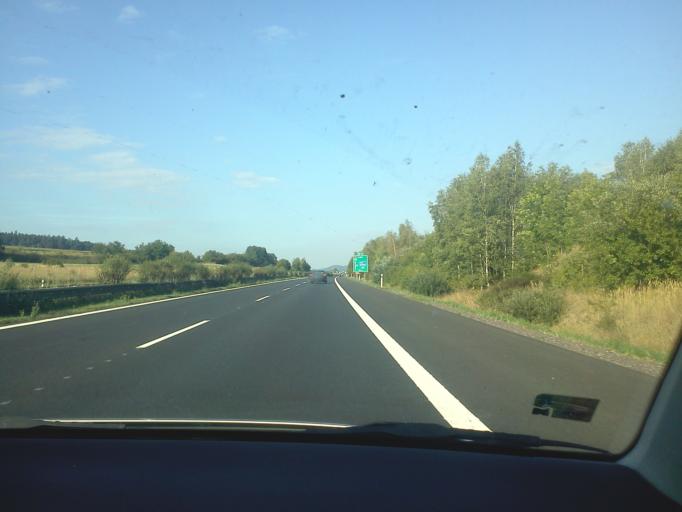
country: CZ
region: Central Bohemia
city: Komarov
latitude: 49.8432
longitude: 13.8317
